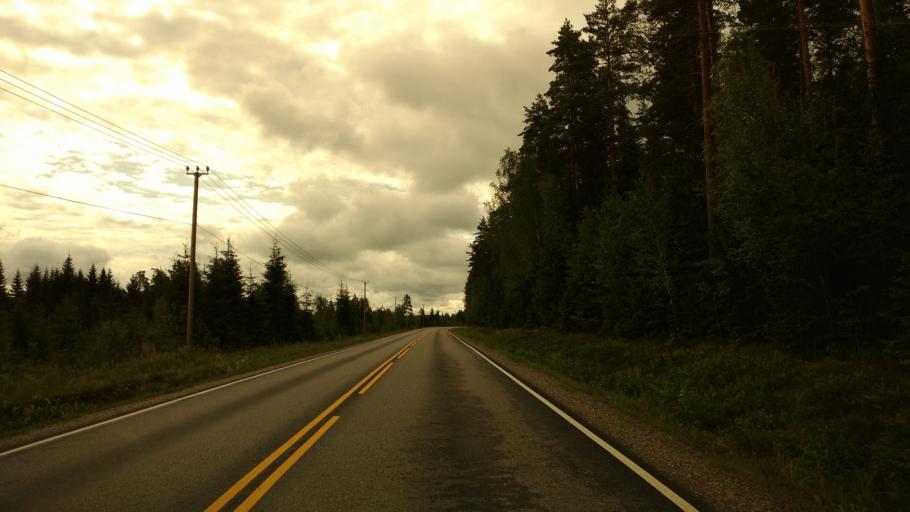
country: FI
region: Varsinais-Suomi
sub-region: Salo
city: Kuusjoki
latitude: 60.4529
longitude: 23.1717
